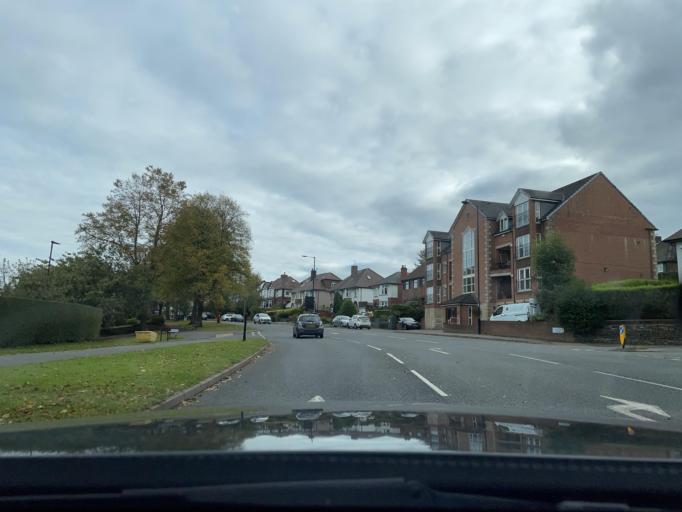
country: GB
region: England
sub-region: Sheffield
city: Oughtibridge
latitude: 53.3805
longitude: -1.5326
